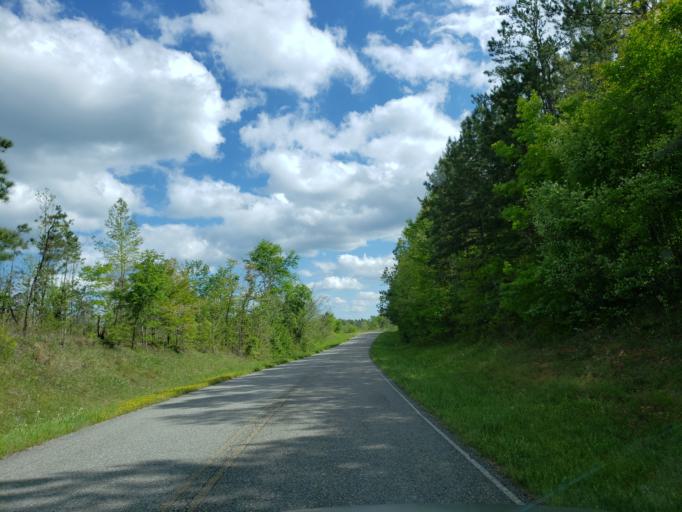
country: US
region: Georgia
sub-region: Haralson County
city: Tallapoosa
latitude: 33.7074
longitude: -85.3801
